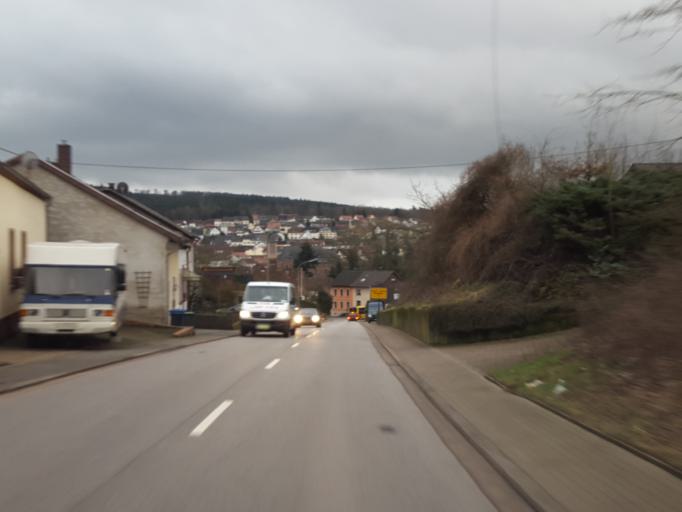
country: DE
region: Saarland
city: Nalbach
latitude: 49.4186
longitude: 6.7633
